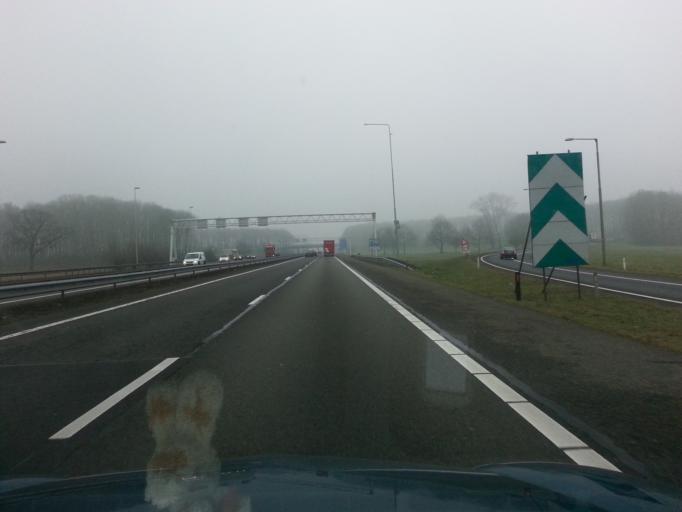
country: NL
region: Gelderland
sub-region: Gemeente Zevenaar
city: Zevenaar
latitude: 51.9165
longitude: 6.1357
